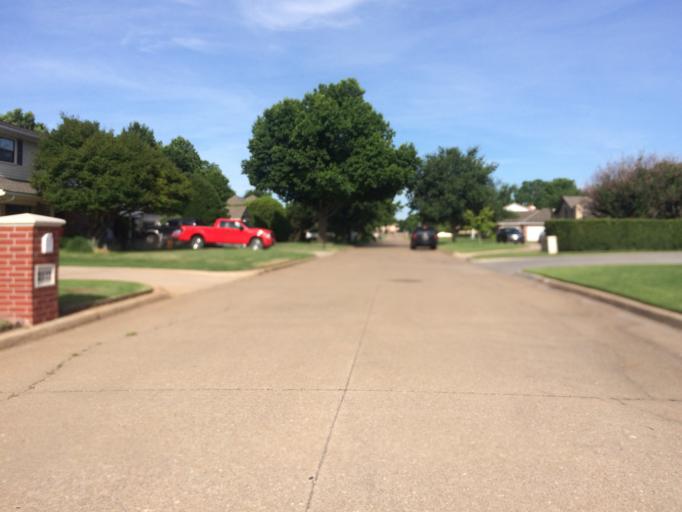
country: US
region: Oklahoma
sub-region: Cleveland County
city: Norman
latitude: 35.2277
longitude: -97.4730
